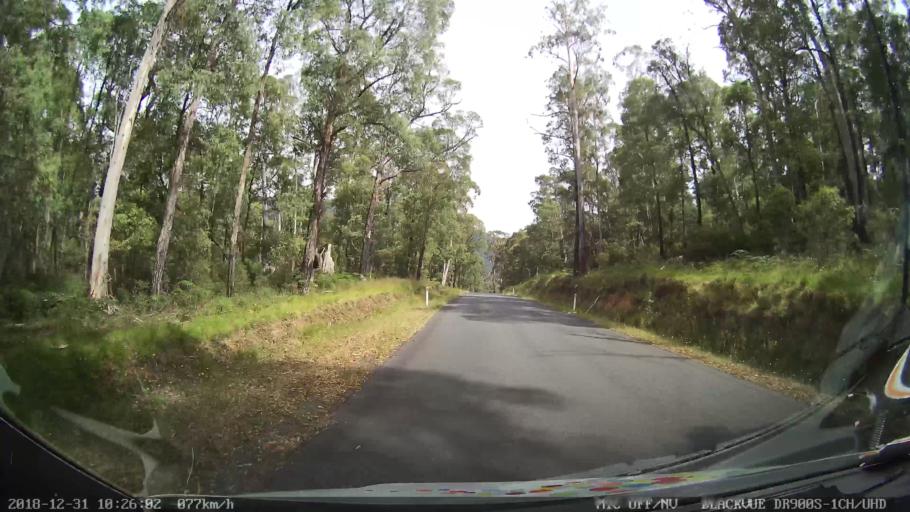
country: AU
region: New South Wales
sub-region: Snowy River
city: Jindabyne
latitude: -36.4995
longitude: 148.1431
